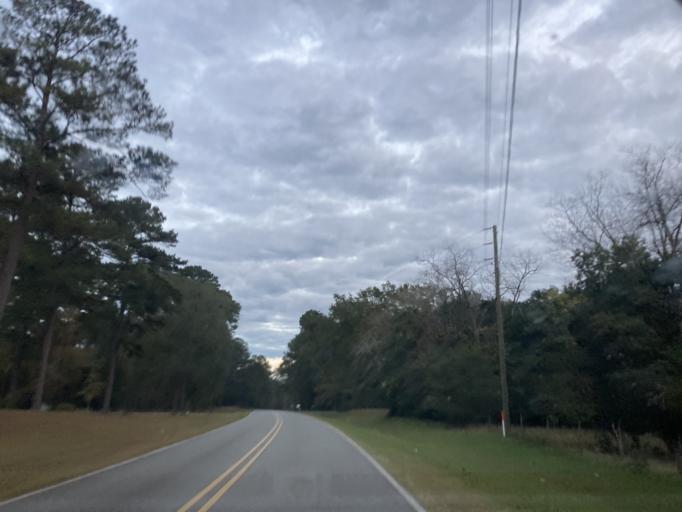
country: US
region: Georgia
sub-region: Jones County
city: Gray
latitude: 32.9738
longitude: -83.5178
